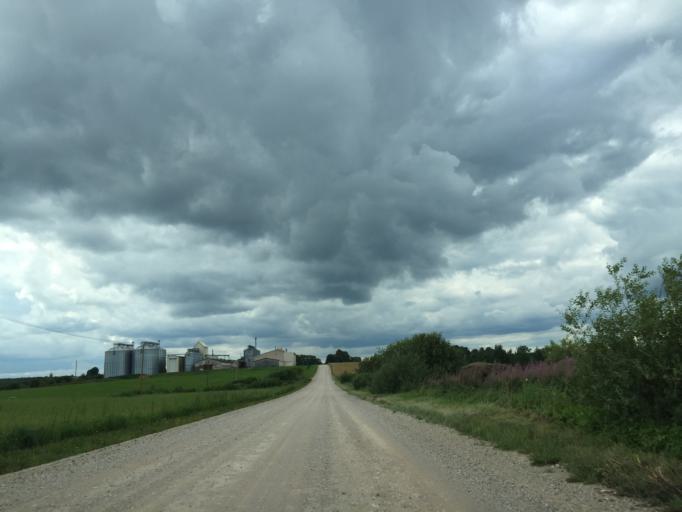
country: LV
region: Malpils
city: Malpils
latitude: 56.8558
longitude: 25.0373
